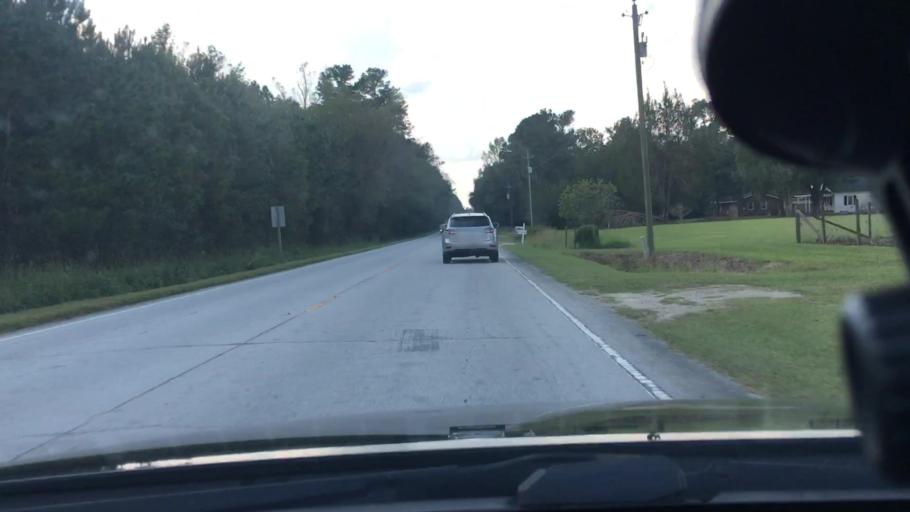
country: US
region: North Carolina
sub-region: Craven County
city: Vanceboro
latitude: 35.3889
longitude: -77.2293
